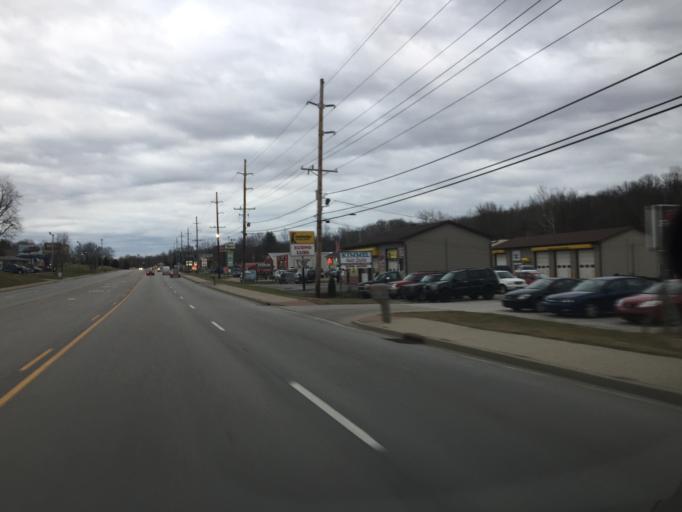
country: US
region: Indiana
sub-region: Monroe County
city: Ellettsville
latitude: 39.2208
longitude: -86.6051
